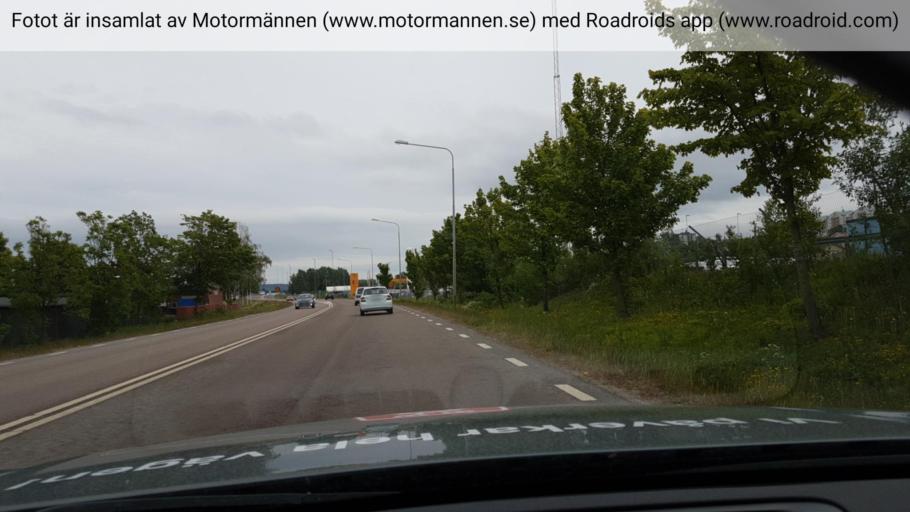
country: SE
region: Vaesternorrland
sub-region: Sundsvalls Kommun
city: Sundsvall
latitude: 62.3861
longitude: 17.3215
